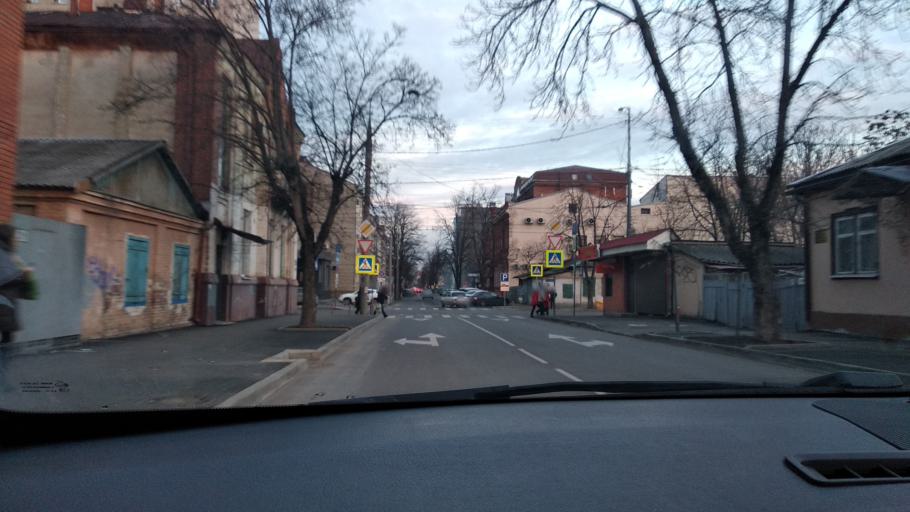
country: RU
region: Krasnodarskiy
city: Krasnodar
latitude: 45.0202
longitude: 38.9637
